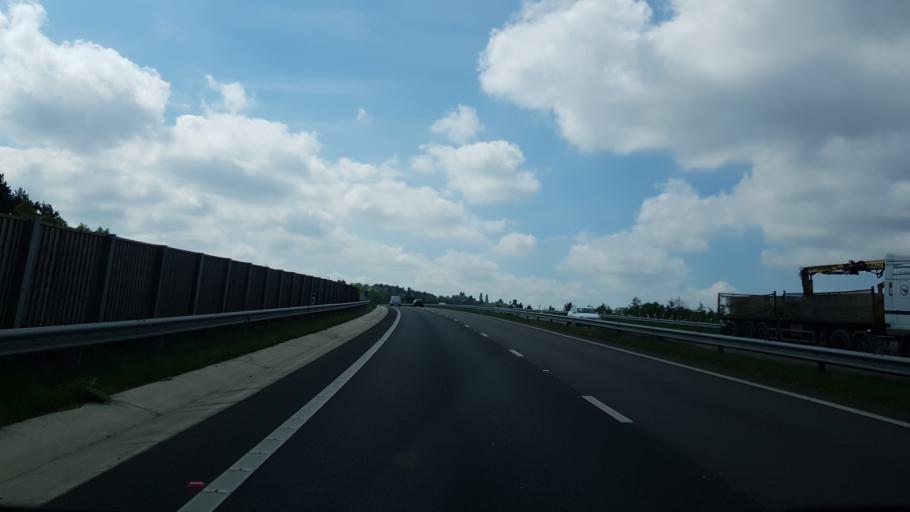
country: GB
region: England
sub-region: Kent
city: Pembury
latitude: 51.1579
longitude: 0.3043
